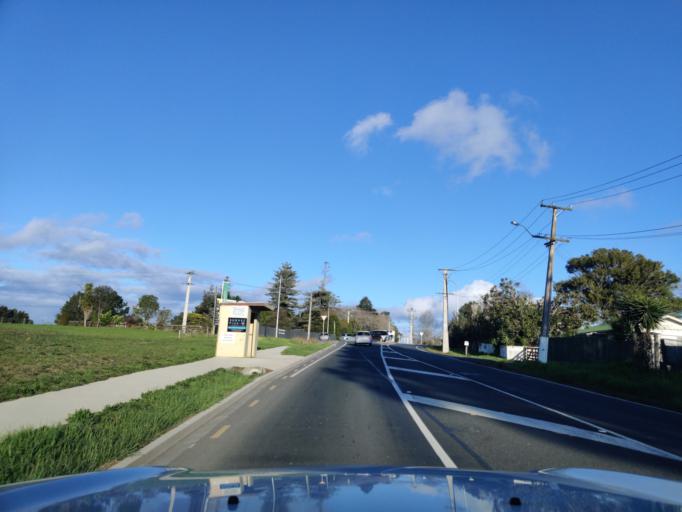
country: NZ
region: Auckland
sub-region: Auckland
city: Pakuranga
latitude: -36.9496
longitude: 174.9658
